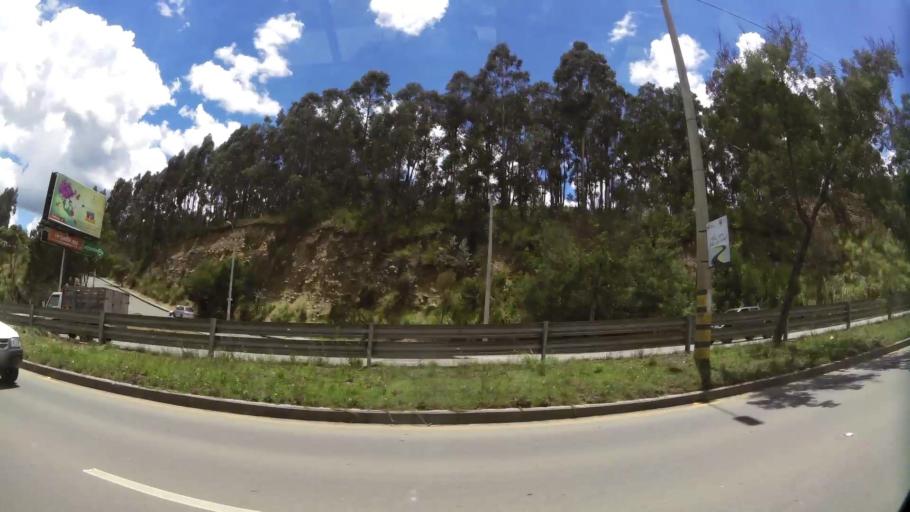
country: EC
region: Azuay
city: Cuenca
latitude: -2.9037
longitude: -78.9770
